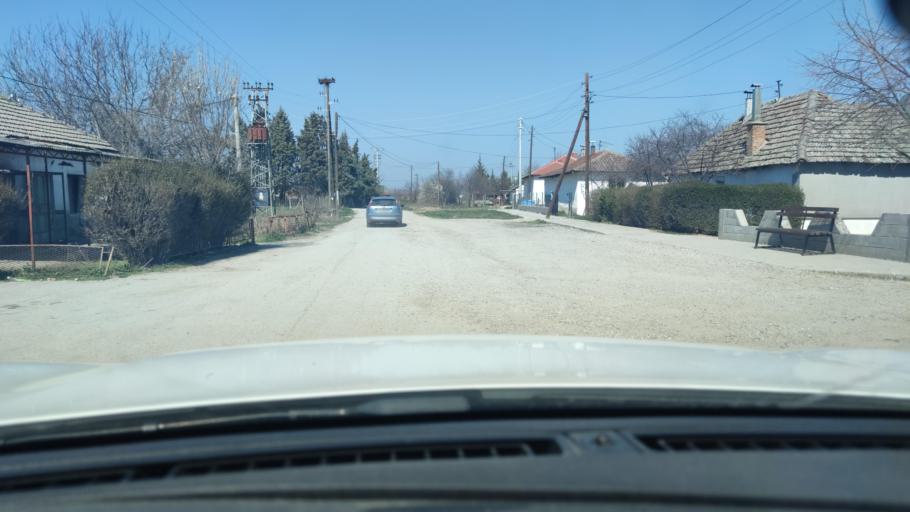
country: MK
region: Rosoman
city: Rosoman
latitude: 41.4746
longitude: 21.9188
